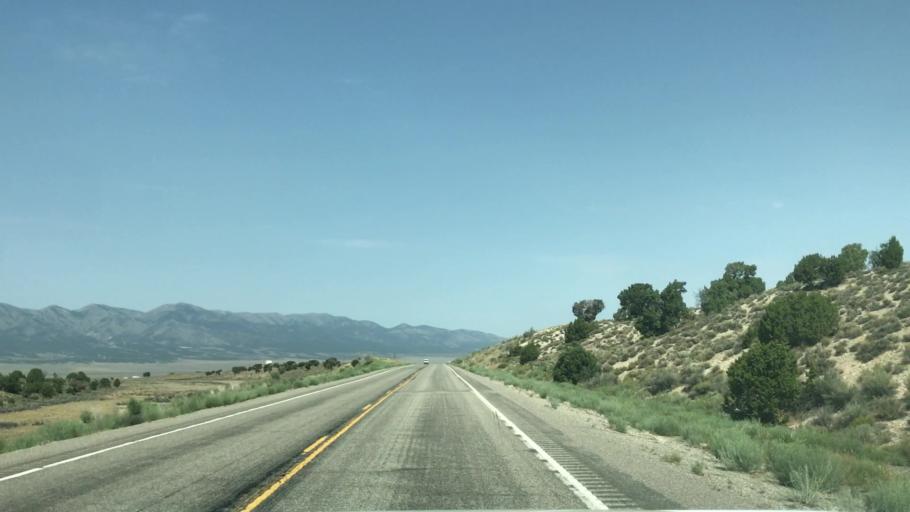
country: US
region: Nevada
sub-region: White Pine County
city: Ely
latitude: 39.0366
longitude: -114.7089
